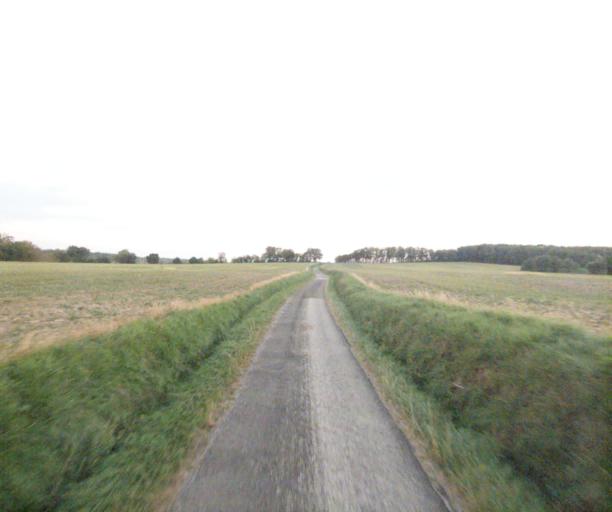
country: FR
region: Midi-Pyrenees
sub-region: Departement du Gers
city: Gondrin
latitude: 43.8163
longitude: 0.2523
